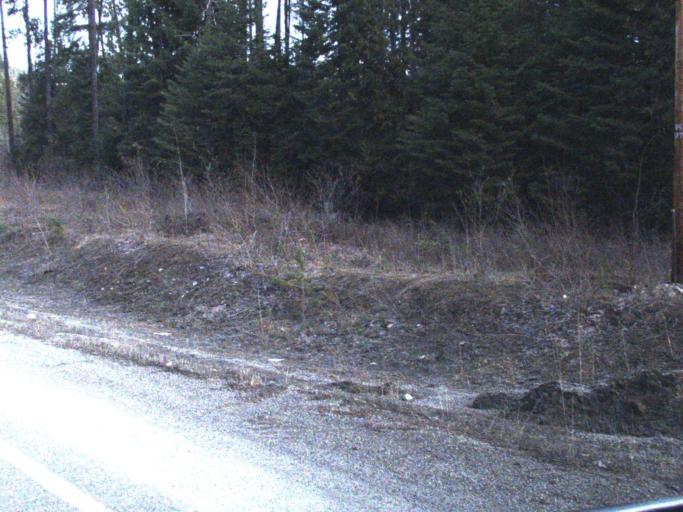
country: US
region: Washington
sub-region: Stevens County
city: Chewelah
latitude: 48.6119
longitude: -117.3656
